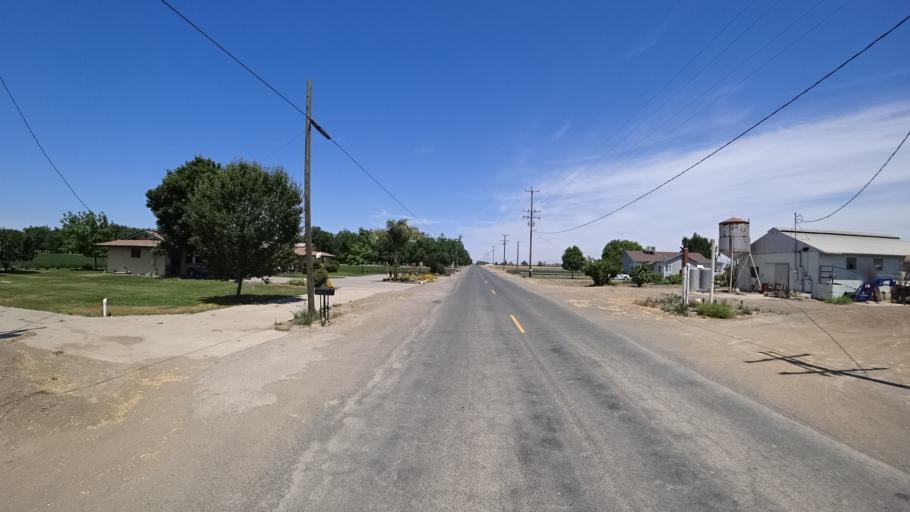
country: US
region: California
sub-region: Kings County
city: Armona
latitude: 36.3344
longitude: -119.7269
